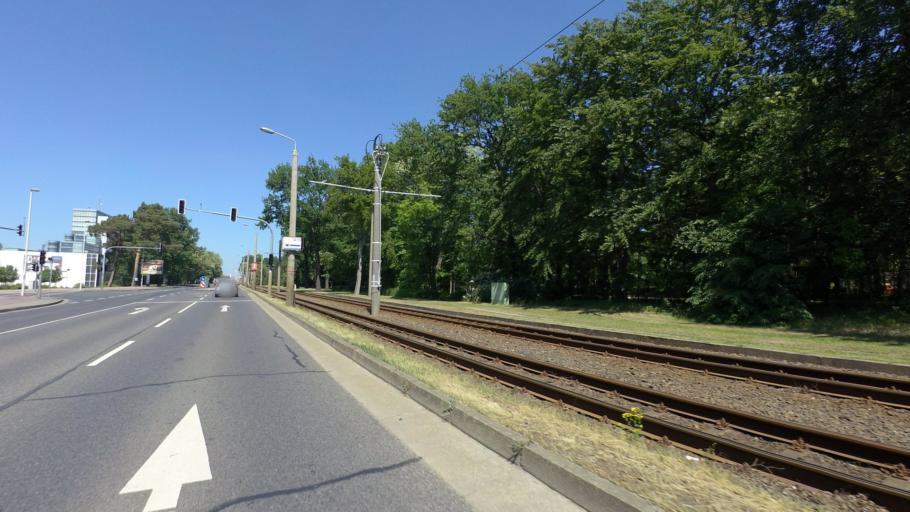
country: DE
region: Brandenburg
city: Cottbus
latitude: 51.7343
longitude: 14.3379
